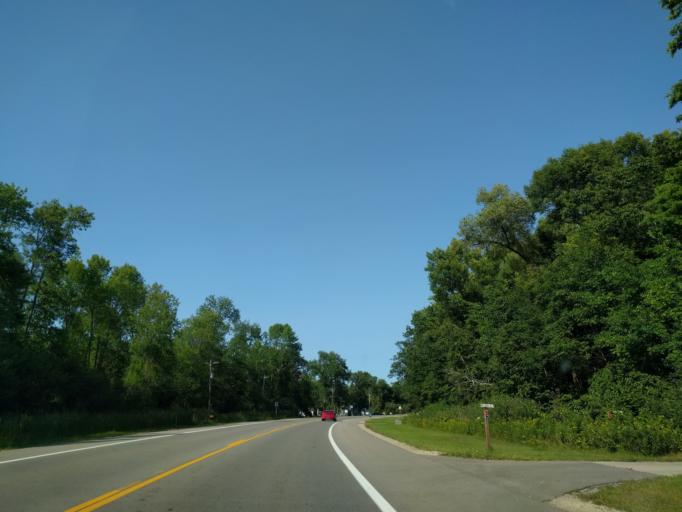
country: US
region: Michigan
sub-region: Menominee County
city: Menominee
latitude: 45.1490
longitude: -87.6026
